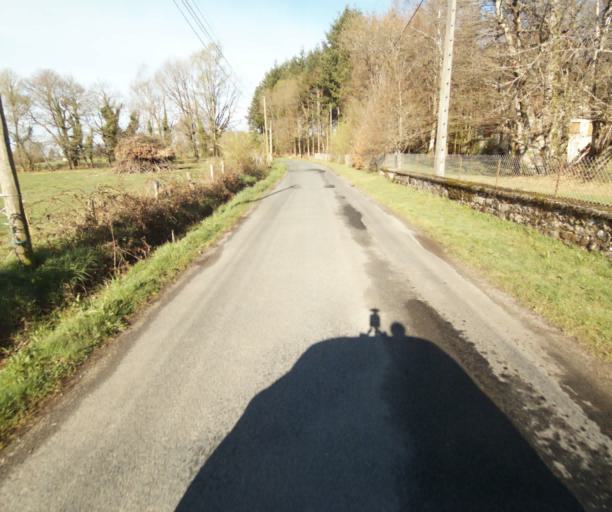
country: FR
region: Limousin
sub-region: Departement de la Correze
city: Laguenne
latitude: 45.2679
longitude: 1.8819
